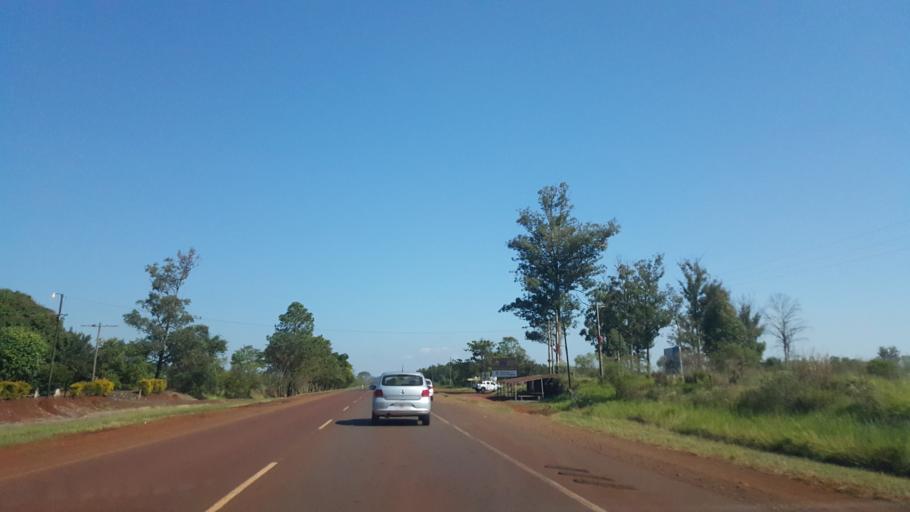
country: AR
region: Misiones
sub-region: Departamento de Capital
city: Posadas
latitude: -27.4217
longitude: -55.9943
